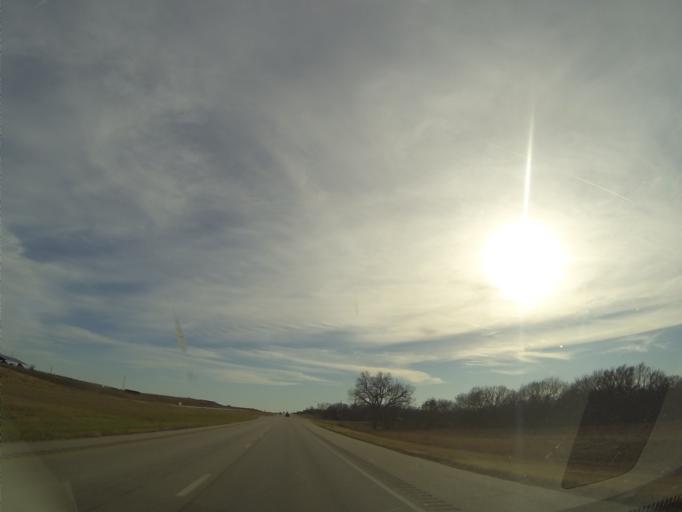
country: US
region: Kansas
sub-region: Ottawa County
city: Minneapolis
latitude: 39.1335
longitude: -97.6693
